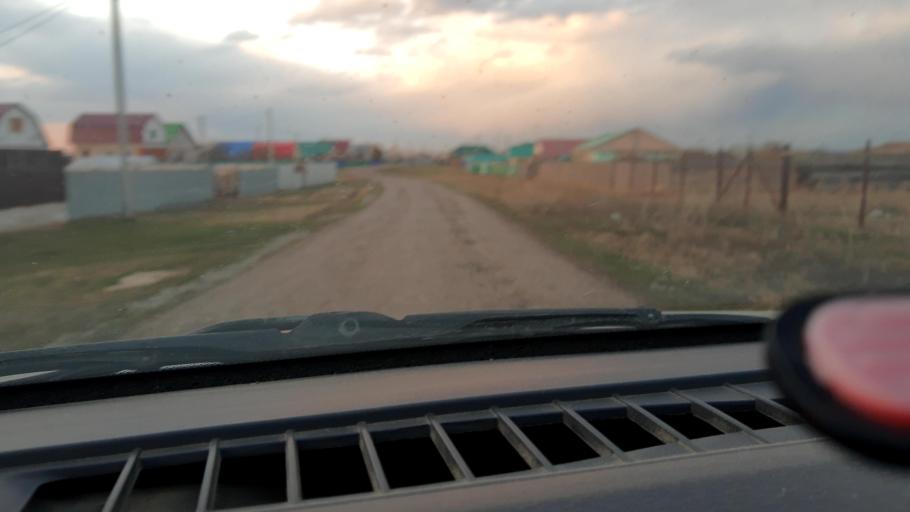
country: RU
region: Bashkortostan
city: Asanovo
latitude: 54.9034
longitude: 55.4846
